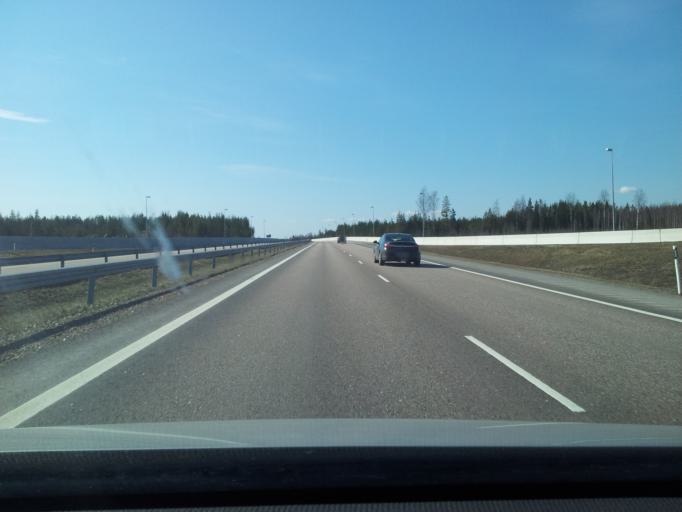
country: FI
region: Kymenlaakso
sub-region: Kotka-Hamina
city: Broby
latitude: 60.5036
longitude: 26.7401
